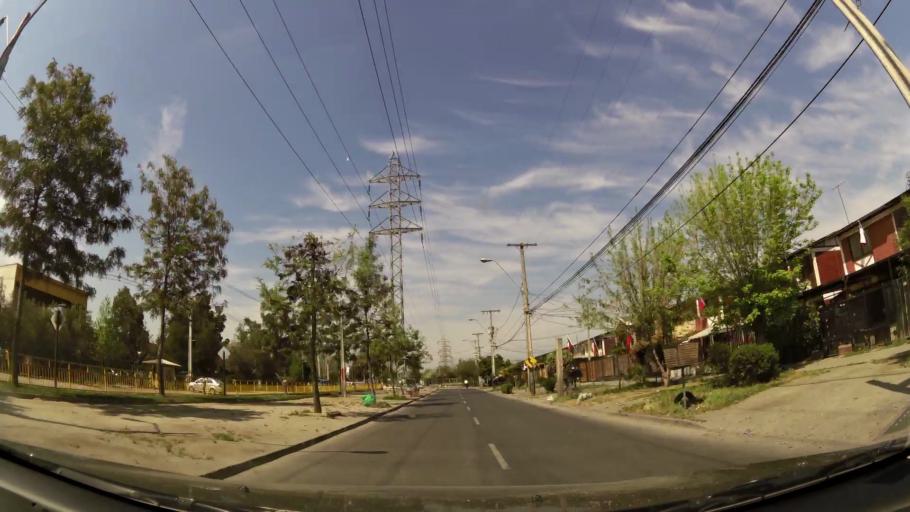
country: CL
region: Santiago Metropolitan
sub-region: Provincia de Santiago
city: La Pintana
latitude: -33.5797
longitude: -70.5981
